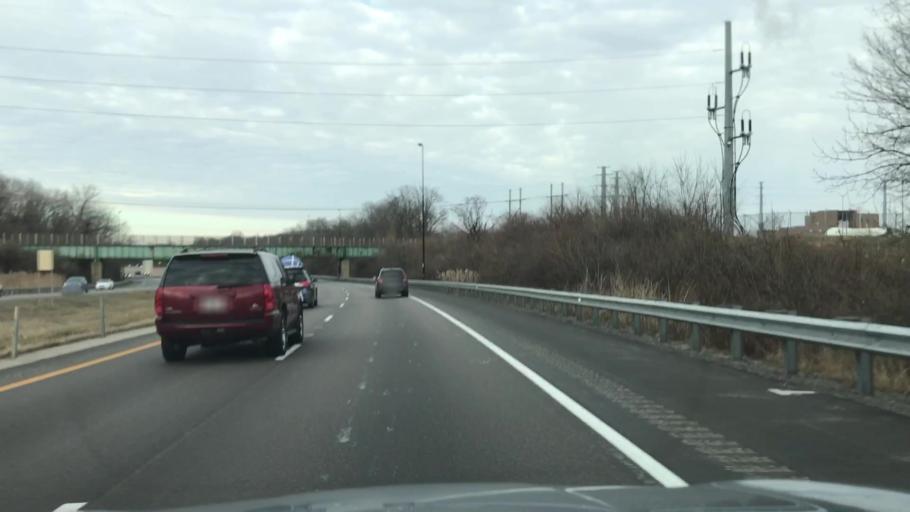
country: US
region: Illinois
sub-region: Sangamon County
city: Southern View
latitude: 39.7556
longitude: -89.6069
